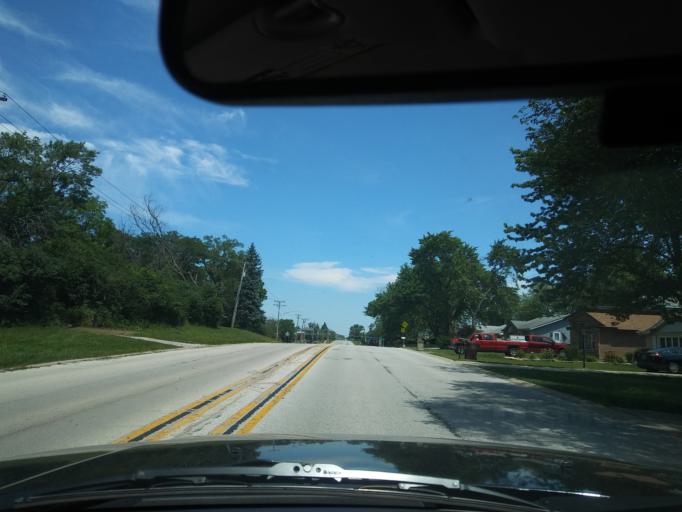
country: US
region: Illinois
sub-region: Cook County
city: Oak Forest
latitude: 41.6006
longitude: -87.7559
